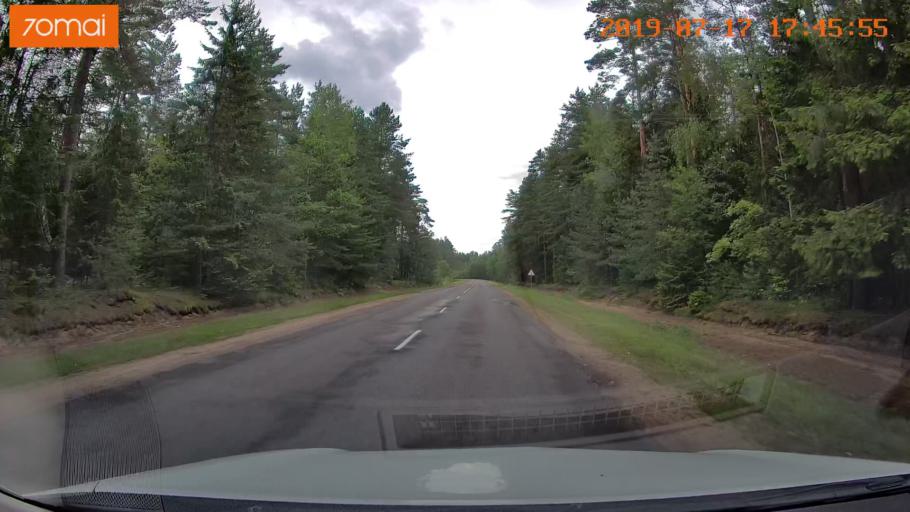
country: BY
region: Mogilev
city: Hlusha
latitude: 53.0923
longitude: 28.8457
